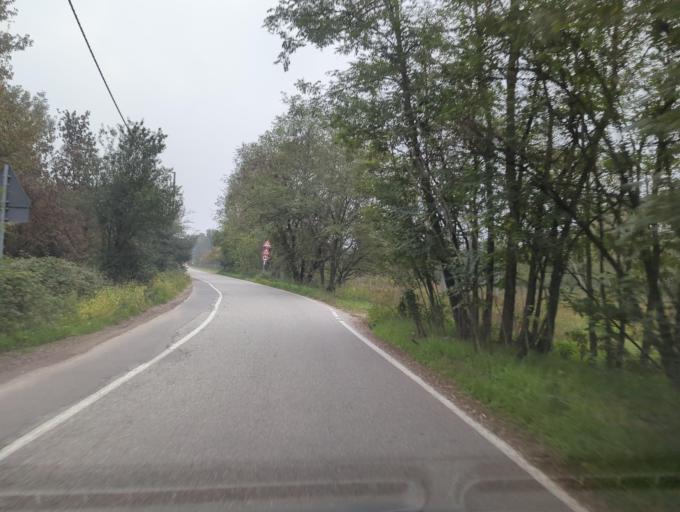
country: IT
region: Lombardy
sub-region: Citta metropolitana di Milano
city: Nosate
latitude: 45.5546
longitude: 8.7376
